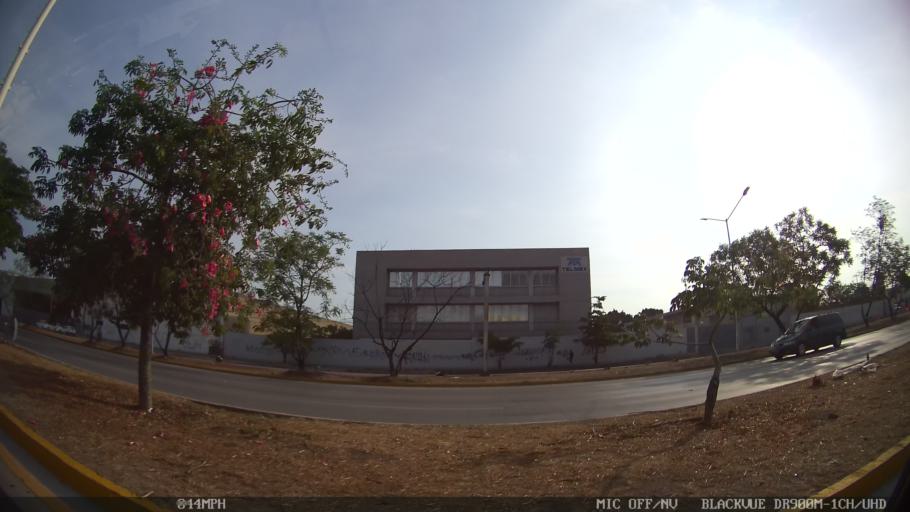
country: MX
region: Jalisco
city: Tlaquepaque
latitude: 20.7146
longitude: -103.3039
